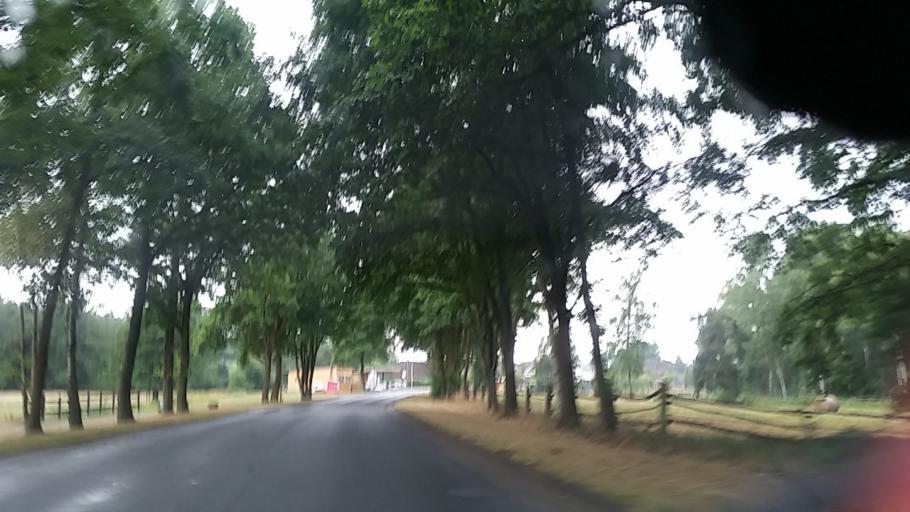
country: DE
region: Lower Saxony
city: Bokensdorf
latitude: 52.4996
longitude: 10.7160
